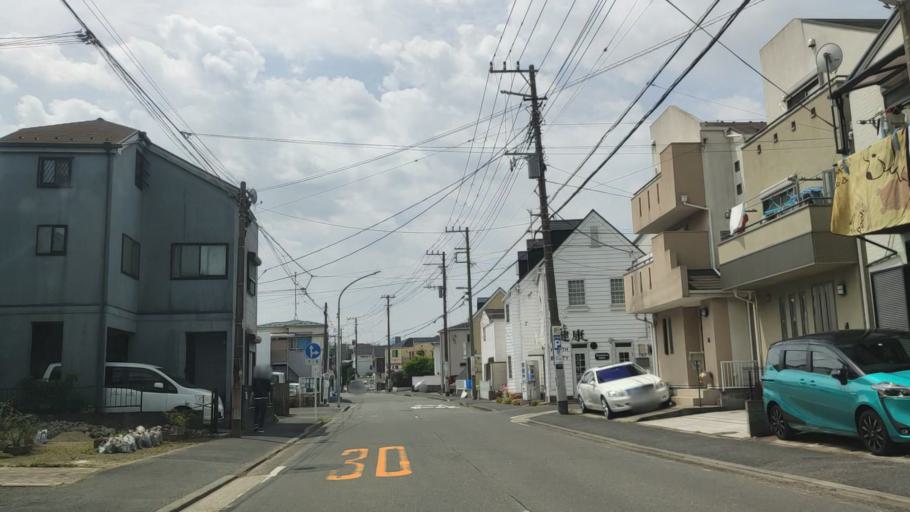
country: JP
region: Kanagawa
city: Yokohama
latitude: 35.4165
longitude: 139.6237
